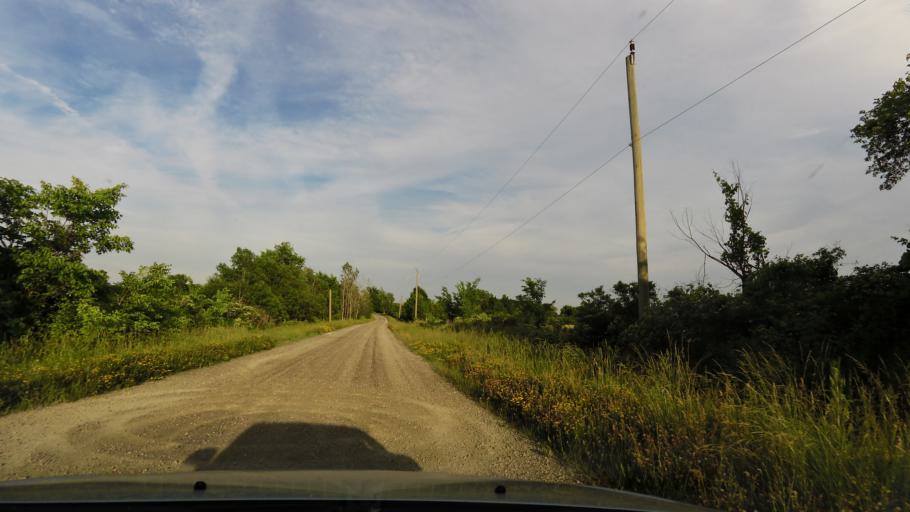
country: CA
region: Ontario
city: Ancaster
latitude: 43.0706
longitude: -79.9682
